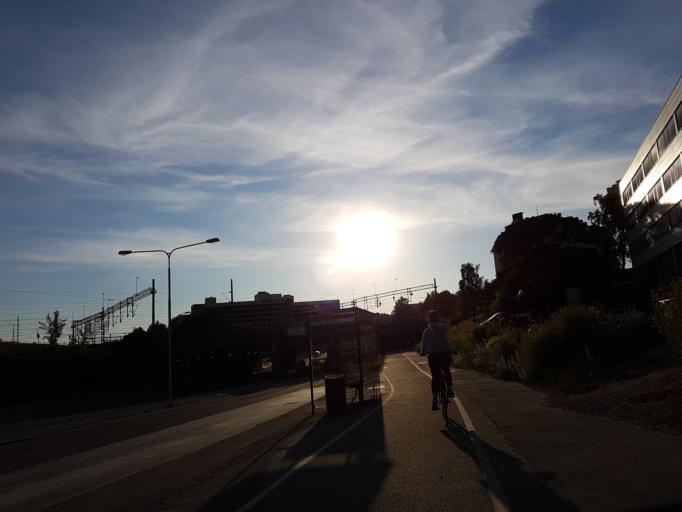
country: SE
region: Stockholm
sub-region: Solna Kommun
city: Solna
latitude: 59.3550
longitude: 18.0154
